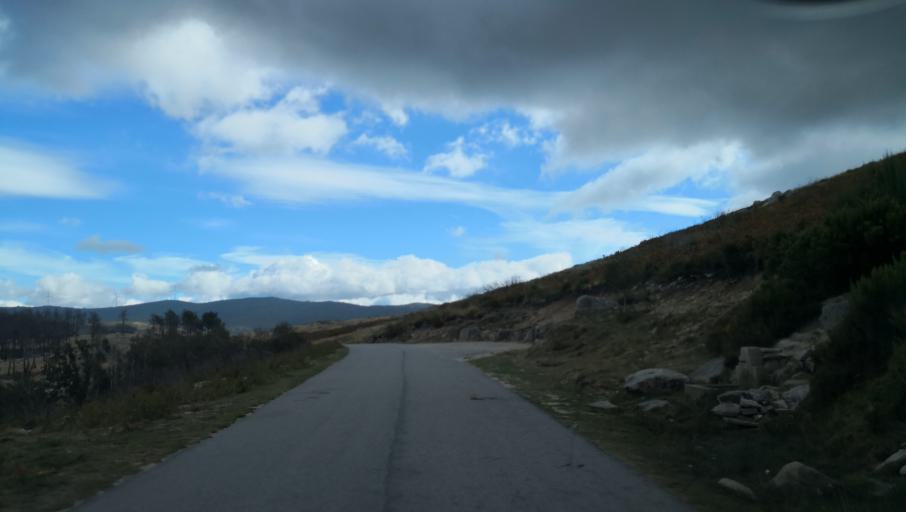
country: PT
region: Vila Real
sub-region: Vila Real
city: Vila Real
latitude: 41.3752
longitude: -7.8219
